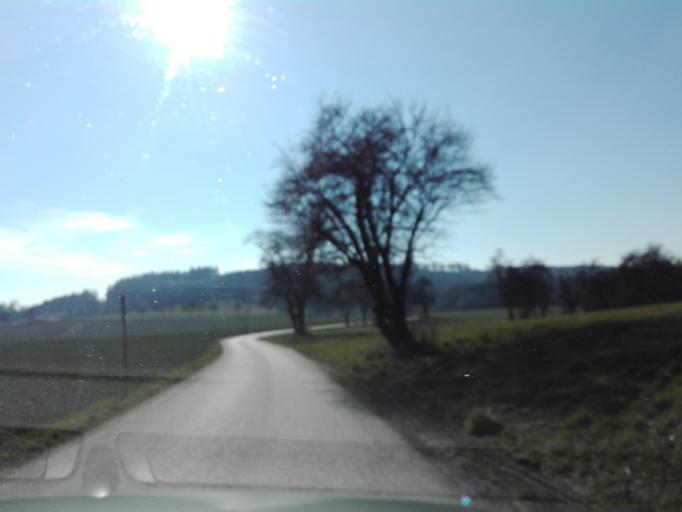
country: AT
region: Upper Austria
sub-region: Wels-Land
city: Holzhausen
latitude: 48.2553
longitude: 14.0892
